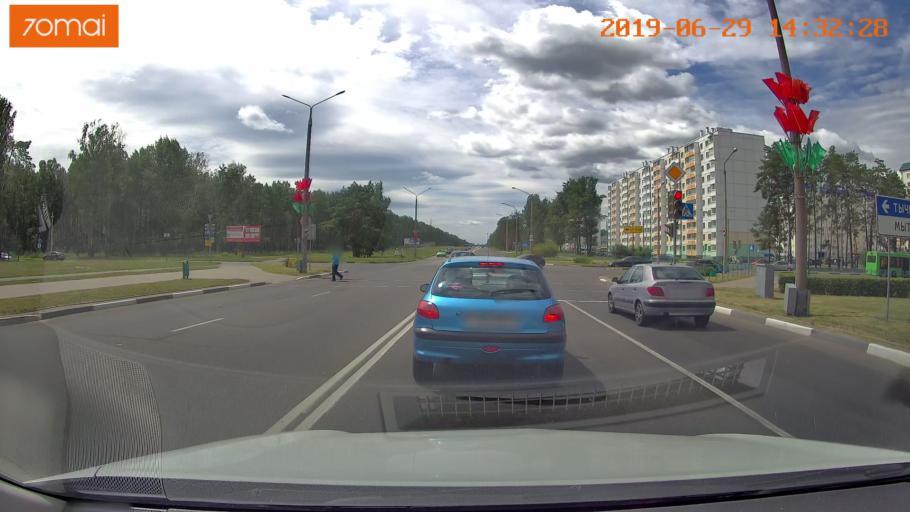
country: BY
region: Minsk
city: Salihorsk
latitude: 52.7815
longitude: 27.5027
